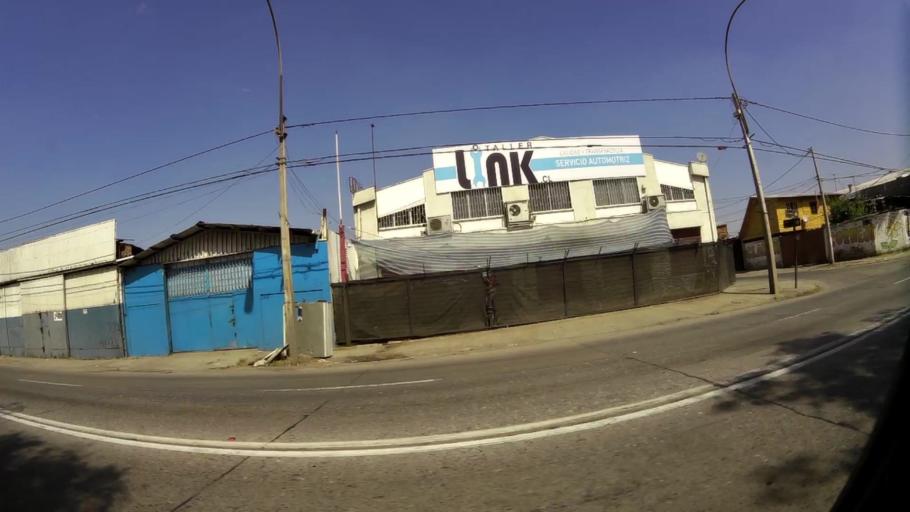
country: CL
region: Santiago Metropolitan
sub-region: Provincia de Santiago
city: Santiago
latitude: -33.4768
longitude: -70.6692
